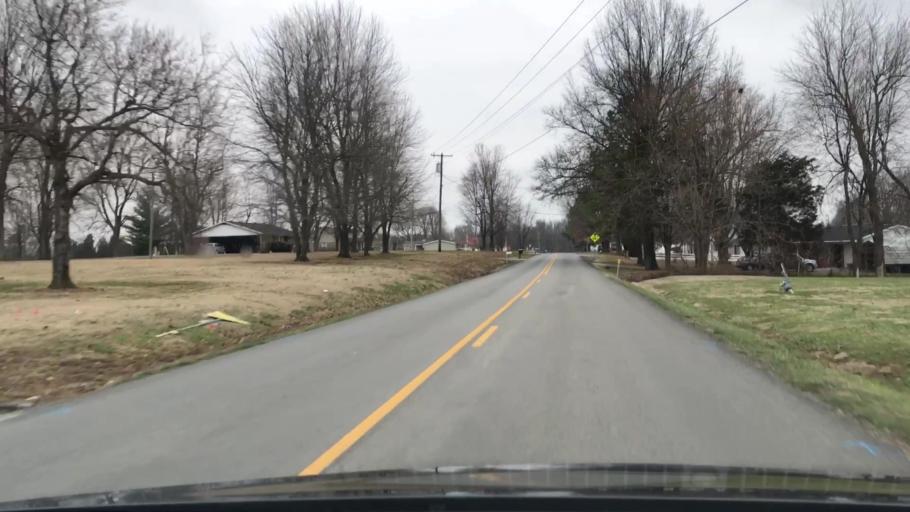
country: US
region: Kentucky
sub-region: Muhlenberg County
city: Morehead
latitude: 37.3403
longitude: -87.2217
